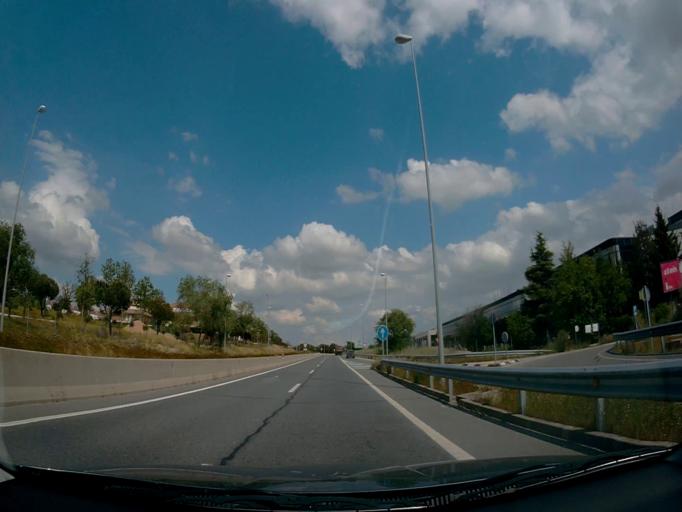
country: ES
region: Madrid
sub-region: Provincia de Madrid
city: Villaviciosa de Odon
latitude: 40.3512
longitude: -3.9069
